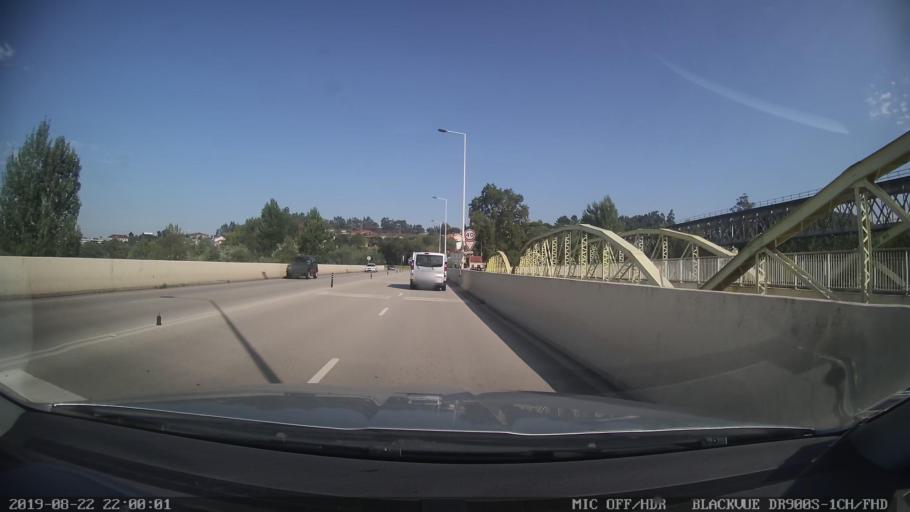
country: PT
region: Coimbra
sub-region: Coimbra
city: Coimbra
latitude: 40.1841
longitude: -8.3961
